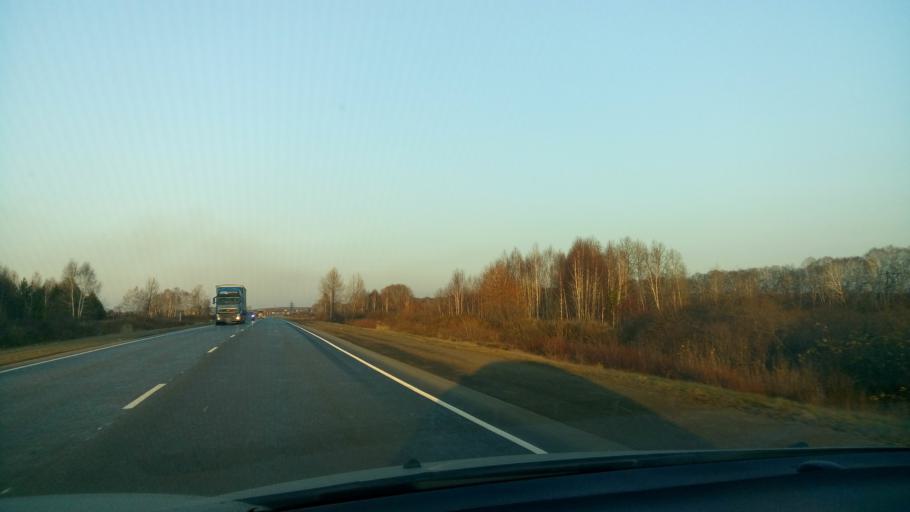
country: RU
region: Sverdlovsk
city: Obukhovskoye
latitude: 56.8334
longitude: 62.5701
